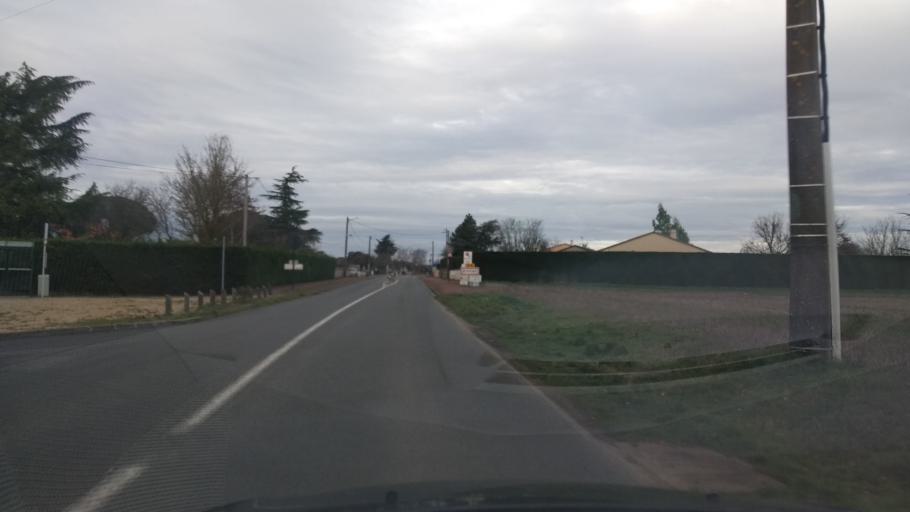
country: FR
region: Poitou-Charentes
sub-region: Departement de la Vienne
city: Dissay
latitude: 46.6876
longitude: 0.4158
